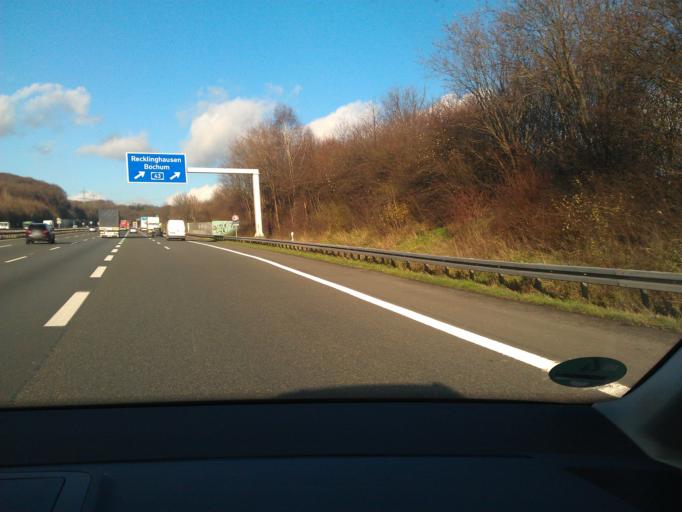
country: DE
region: North Rhine-Westphalia
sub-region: Regierungsbezirk Arnsberg
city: Schwelm
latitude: 51.2997
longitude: 7.2625
